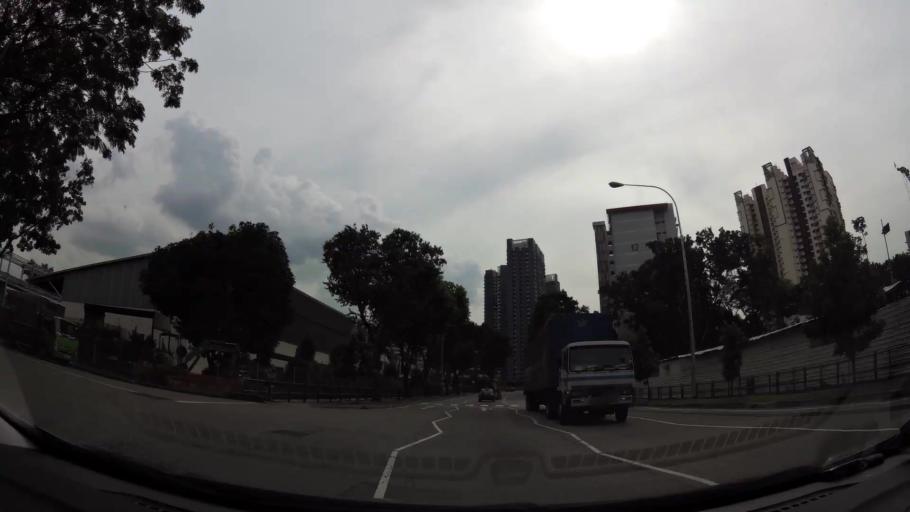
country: MY
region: Johor
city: Johor Bahru
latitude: 1.4418
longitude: 103.7802
